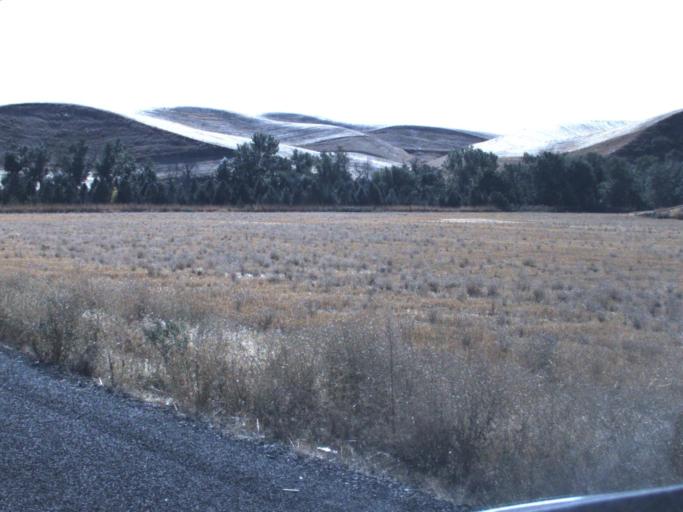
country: US
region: Washington
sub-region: Walla Walla County
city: Waitsburg
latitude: 46.2968
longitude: -118.3408
